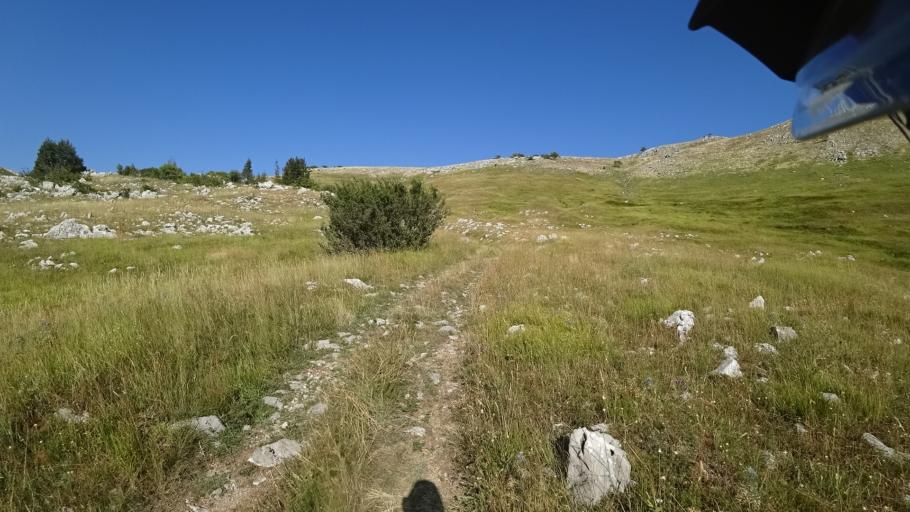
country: HR
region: Sibensko-Kniniska
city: Knin
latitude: 44.2048
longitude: 16.1482
